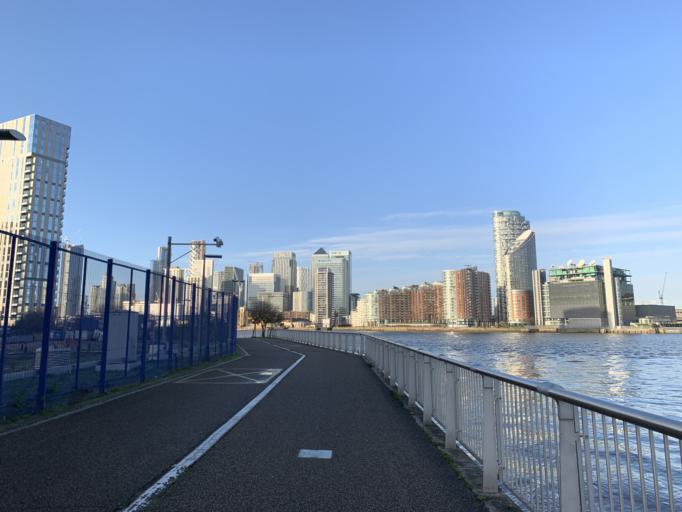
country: GB
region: England
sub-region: Greater London
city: Poplar
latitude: 51.5049
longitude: 0.0031
